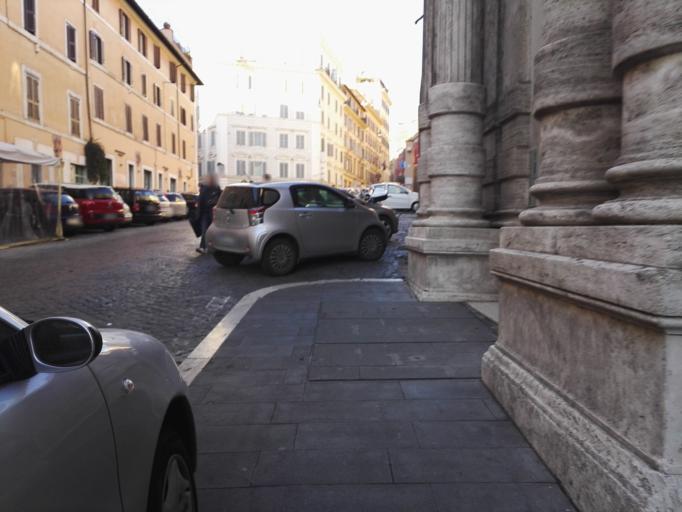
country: IT
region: Latium
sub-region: Citta metropolitana di Roma Capitale
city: Rome
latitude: 41.9035
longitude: 12.4855
